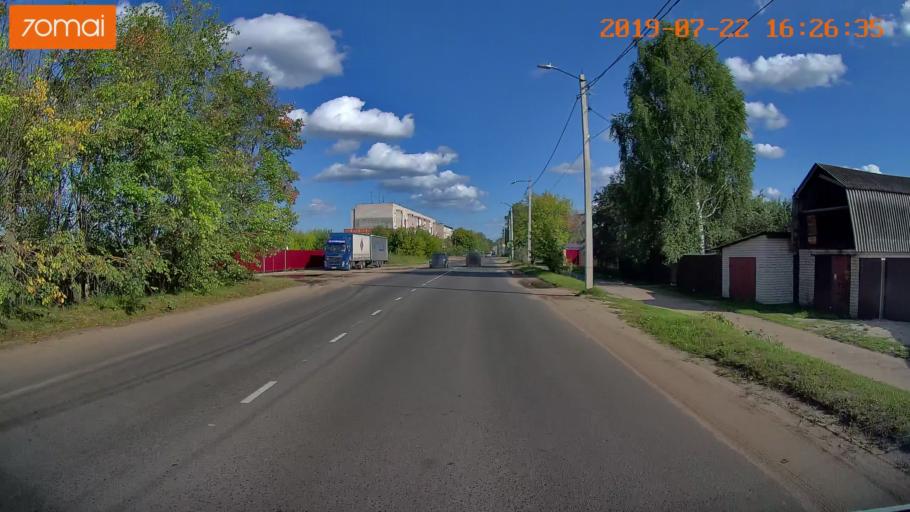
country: RU
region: Ivanovo
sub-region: Gorod Ivanovo
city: Ivanovo
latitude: 57.0484
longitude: 40.9360
